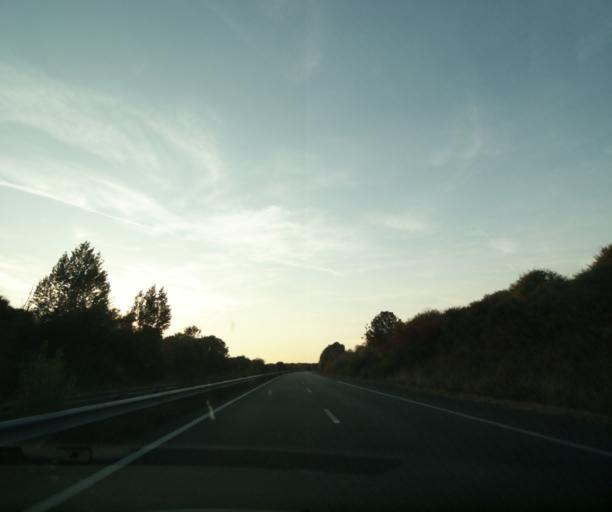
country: FR
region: Aquitaine
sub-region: Departement du Lot-et-Garonne
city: Fourques-sur-Garonne
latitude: 44.3801
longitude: 0.2127
